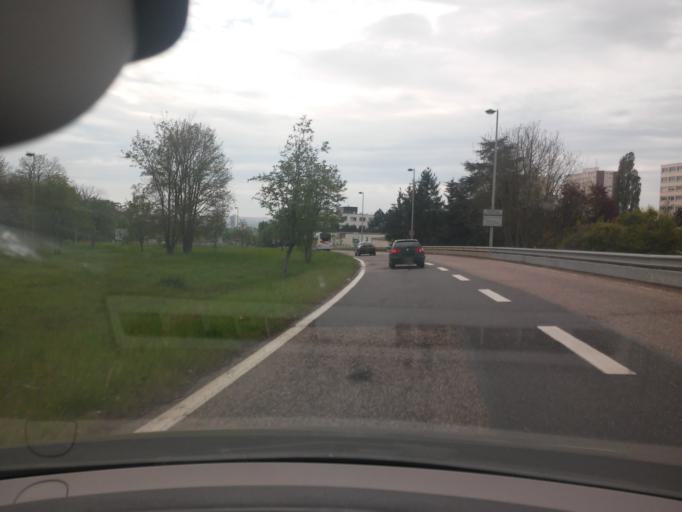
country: FR
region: Lorraine
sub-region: Departement de Meurthe-et-Moselle
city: Laxou
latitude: 48.7038
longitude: 6.1347
